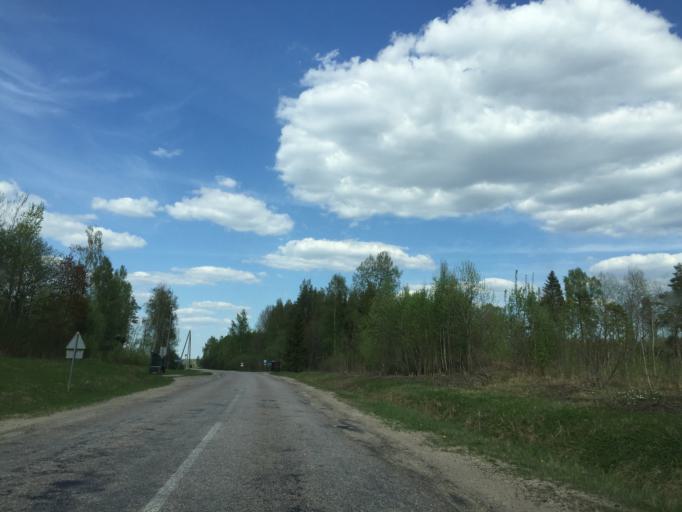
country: LV
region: Limbazu Rajons
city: Limbazi
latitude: 57.4213
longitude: 24.7045
